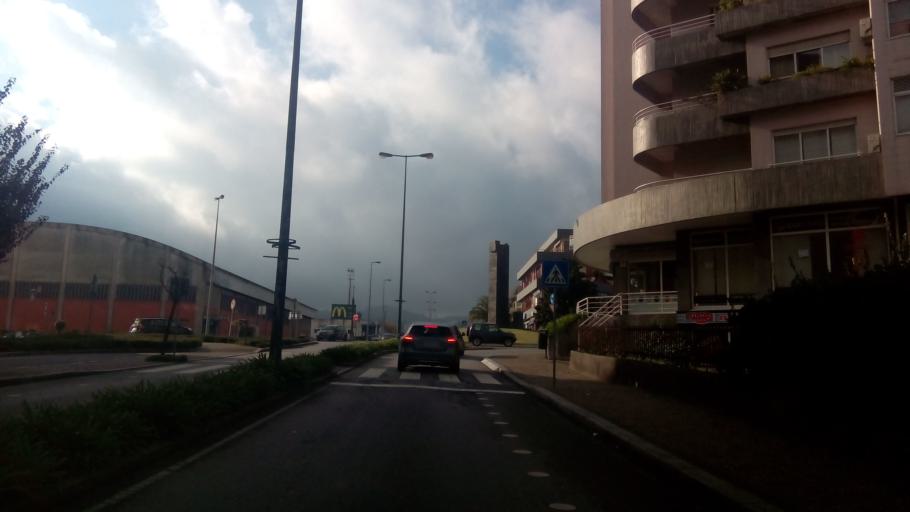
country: PT
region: Porto
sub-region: Paredes
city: Paredes
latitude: 41.2030
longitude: -8.3303
